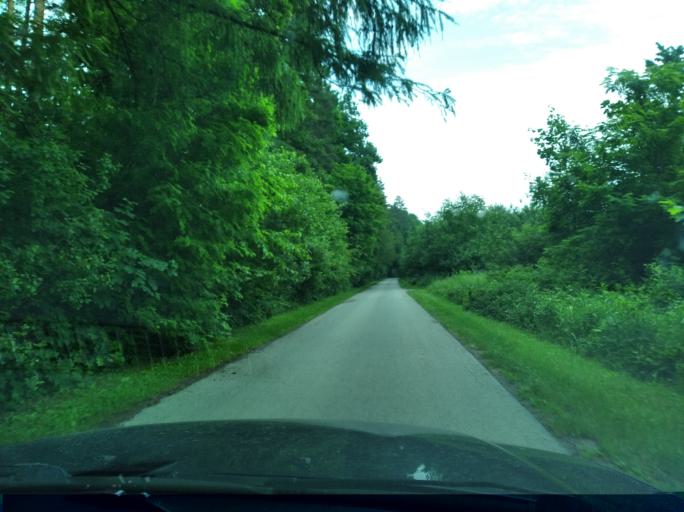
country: PL
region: Subcarpathian Voivodeship
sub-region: Powiat jaroslawski
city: Pruchnik
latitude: 49.8891
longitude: 22.5244
